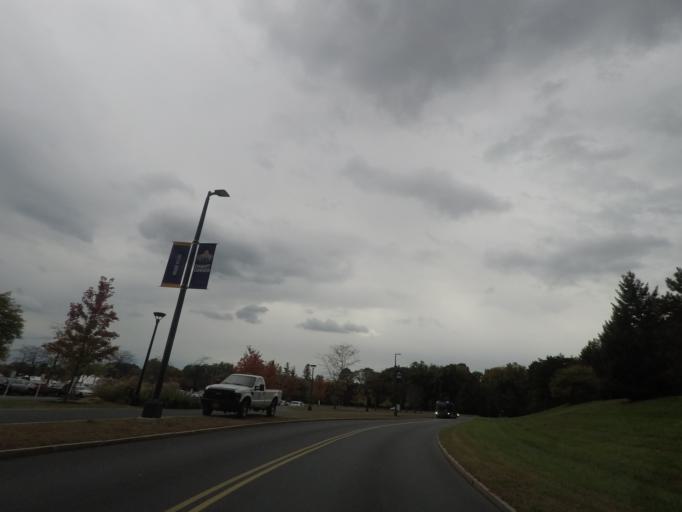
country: US
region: New York
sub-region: Albany County
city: McKownville
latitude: 42.6820
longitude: -73.8293
